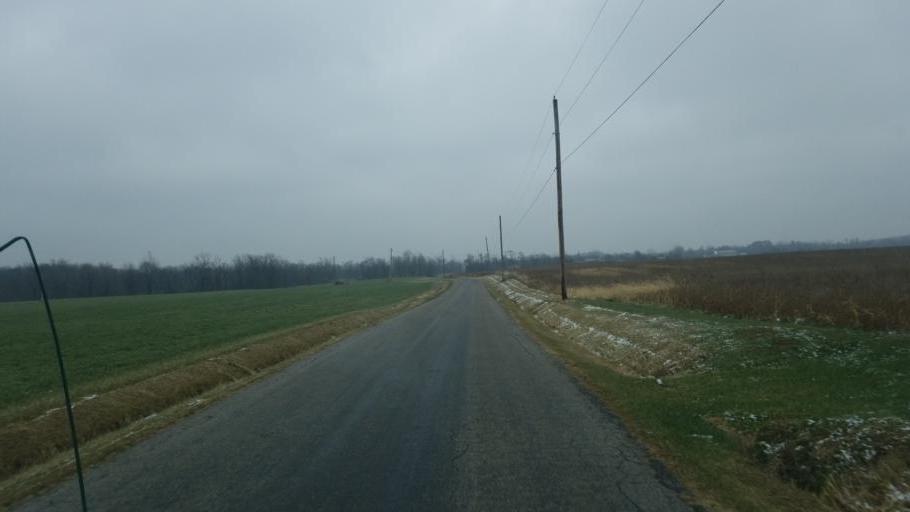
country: US
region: Ohio
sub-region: Huron County
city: New London
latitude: 41.0159
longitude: -82.3376
